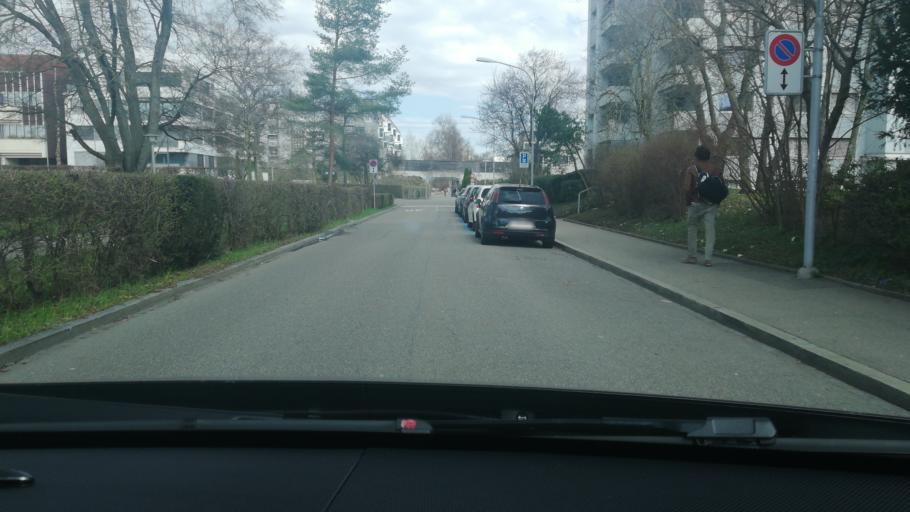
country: CH
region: Zurich
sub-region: Bezirk Zuerich
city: Zuerich (Kreis 12) / Saatlen
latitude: 47.4117
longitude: 8.5588
